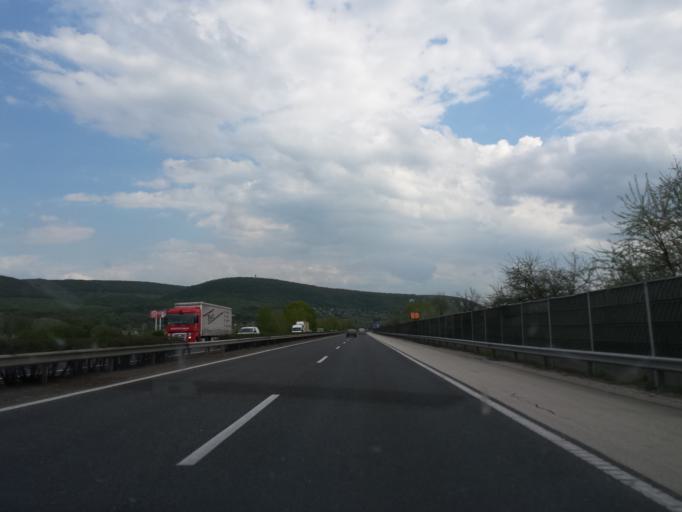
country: HU
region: Komarom-Esztergom
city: Vertesszolos
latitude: 47.6051
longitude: 18.3740
